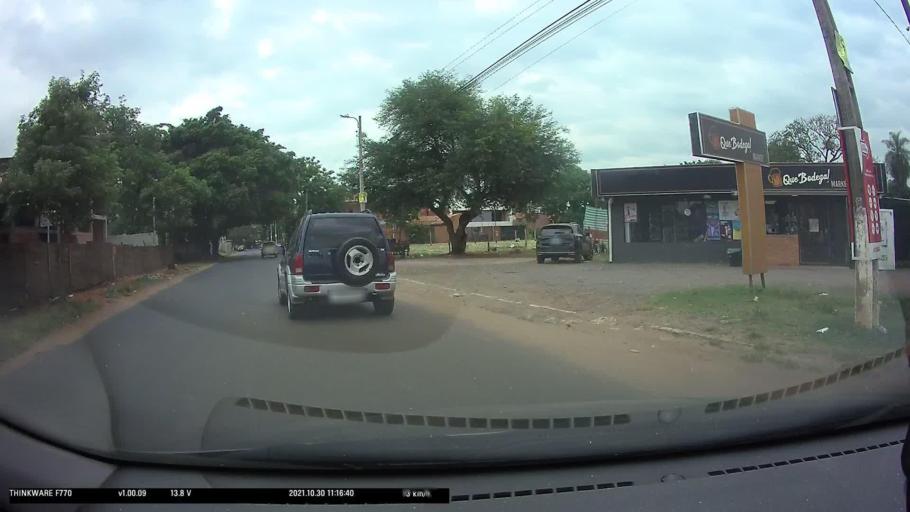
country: PY
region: Central
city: Fernando de la Mora
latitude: -25.3127
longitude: -57.5171
